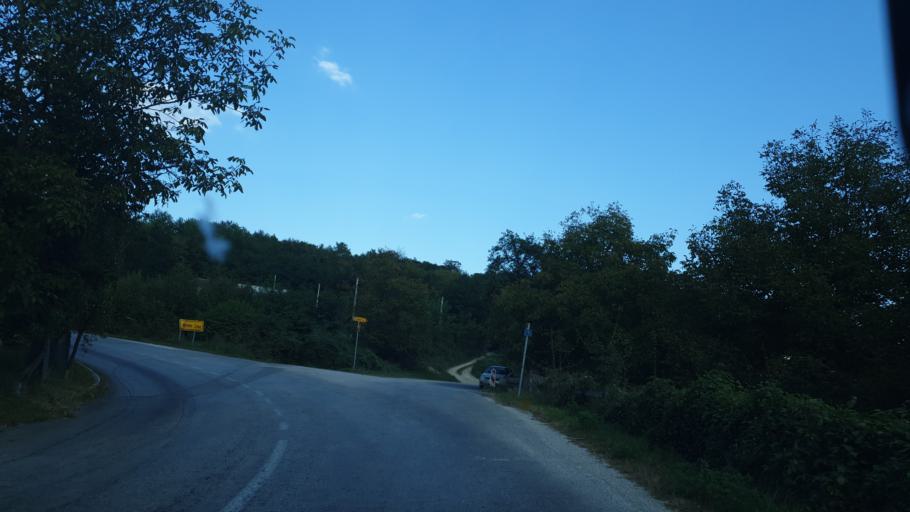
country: RS
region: Central Serbia
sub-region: Zlatiborski Okrug
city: Uzice
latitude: 43.8608
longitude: 19.9045
